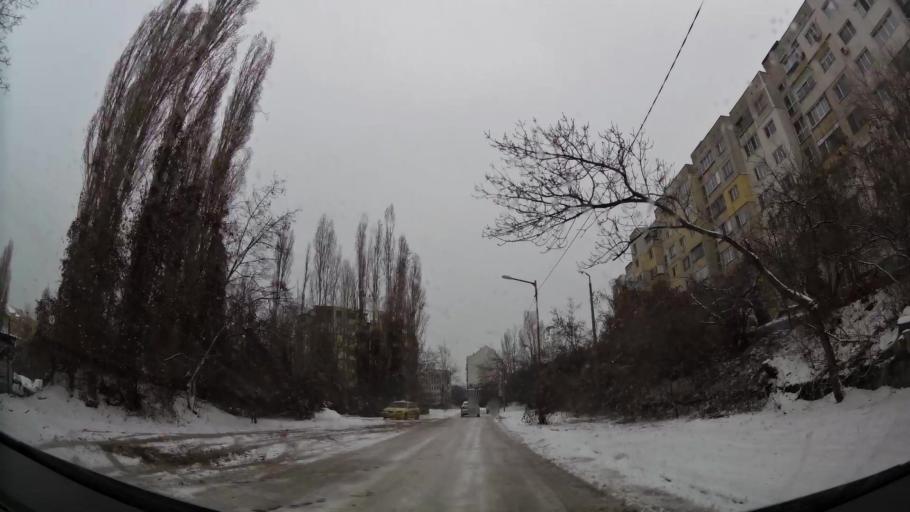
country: BG
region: Sofia-Capital
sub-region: Stolichna Obshtina
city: Sofia
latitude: 42.6957
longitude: 23.3108
